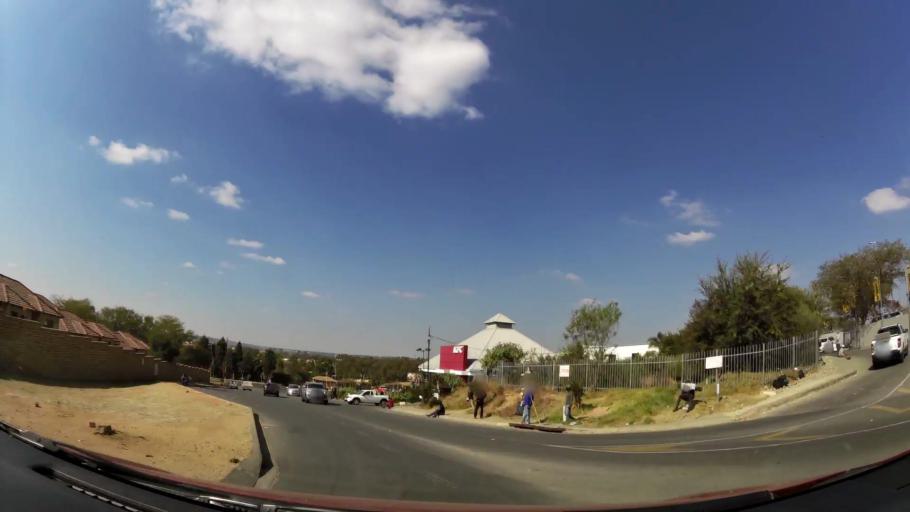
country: ZA
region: Gauteng
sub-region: West Rand District Municipality
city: Muldersdriseloop
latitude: -26.0539
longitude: 27.9542
